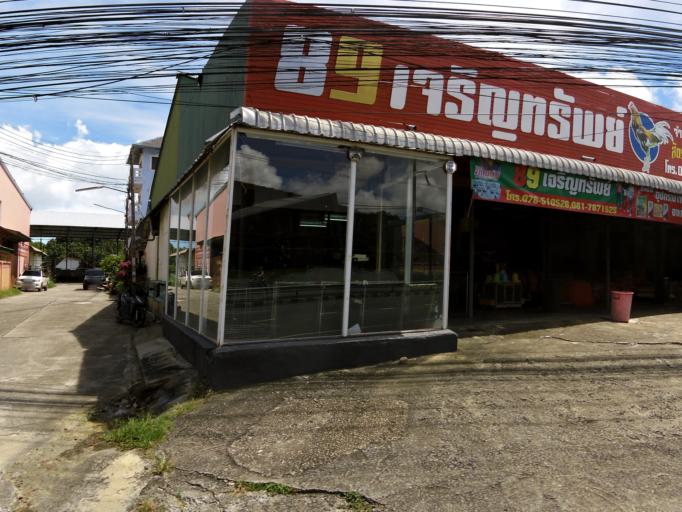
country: TH
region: Phuket
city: Mueang Phuket
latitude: 7.8673
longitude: 98.3517
